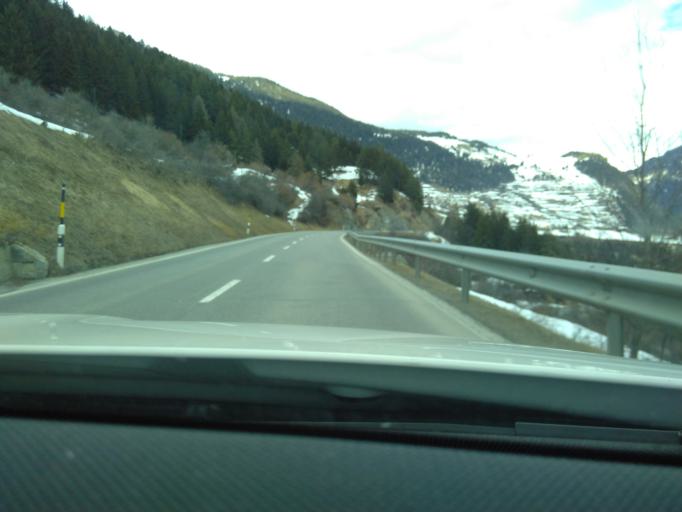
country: CH
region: Grisons
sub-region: Inn District
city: Scuol
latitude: 46.8217
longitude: 10.3627
